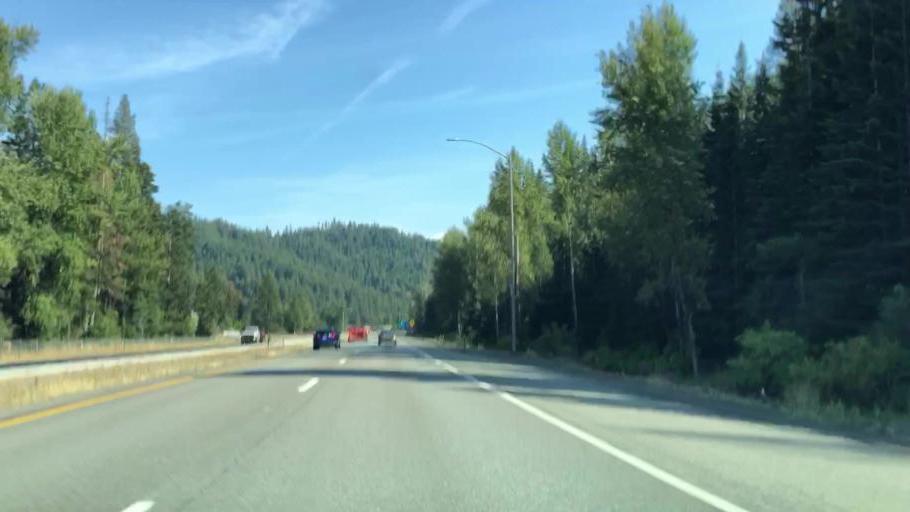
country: US
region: Idaho
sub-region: Shoshone County
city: Pinehurst
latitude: 47.5776
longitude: -116.4533
